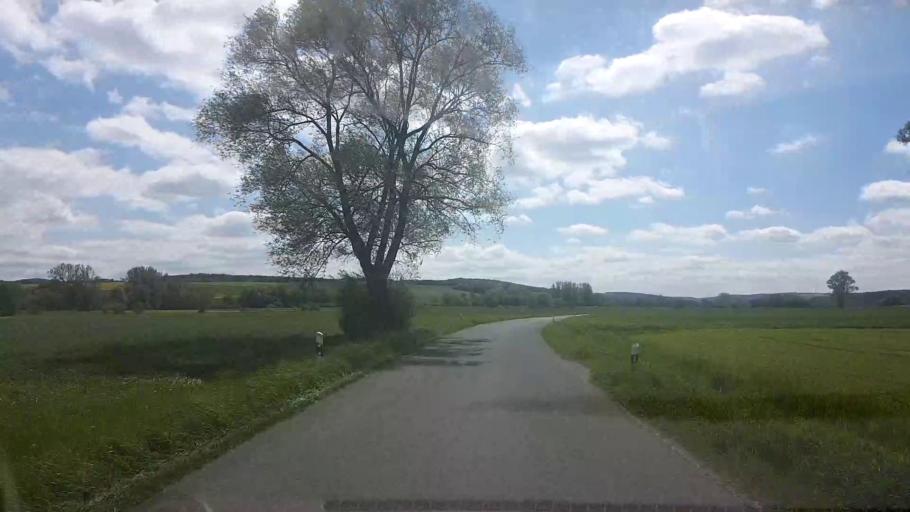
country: DE
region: Bavaria
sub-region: Upper Franconia
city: Grossheirath
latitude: 50.1622
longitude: 10.9282
